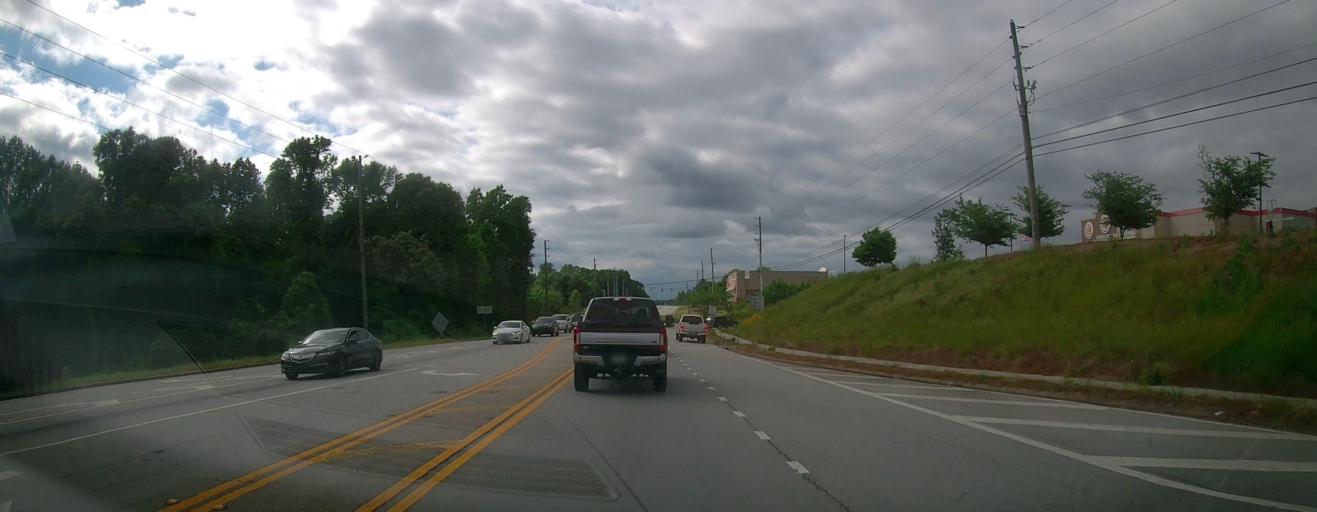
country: US
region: Georgia
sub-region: Walton County
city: Monroe
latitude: 33.7967
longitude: -83.7442
